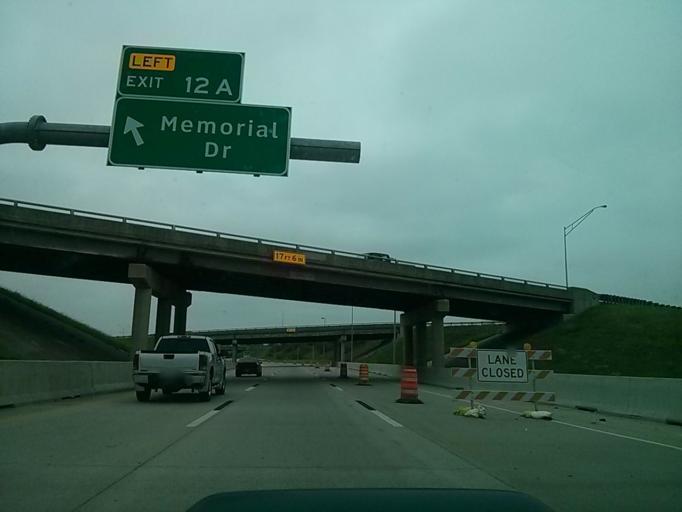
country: US
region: Oklahoma
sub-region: Tulsa County
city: Owasso
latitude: 36.1629
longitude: -95.8816
